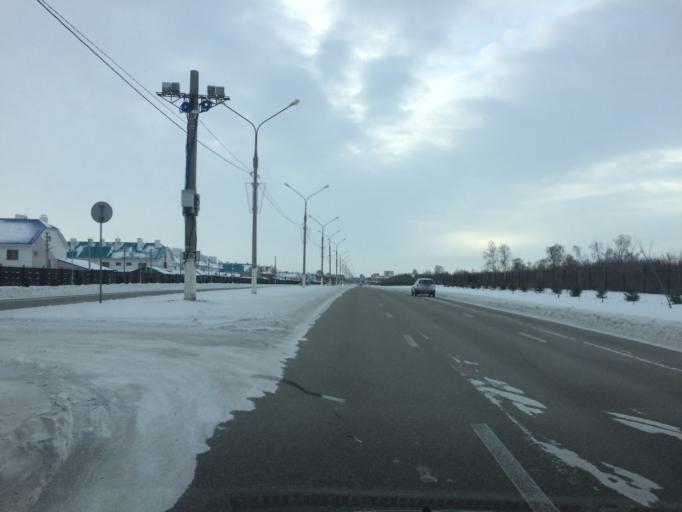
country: RU
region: Chelyabinsk
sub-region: Gorod Magnitogorsk
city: Magnitogorsk
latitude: 53.3820
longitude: 58.9616
